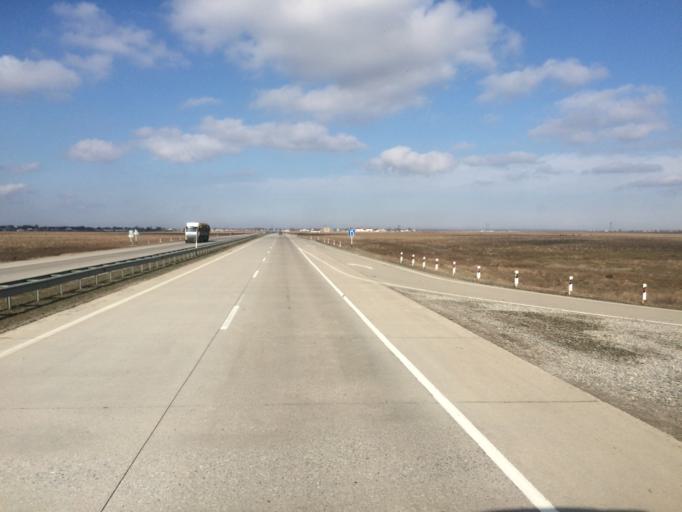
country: KZ
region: Ongtustik Qazaqstan
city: Temirlanovka
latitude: 42.7757
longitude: 69.2063
